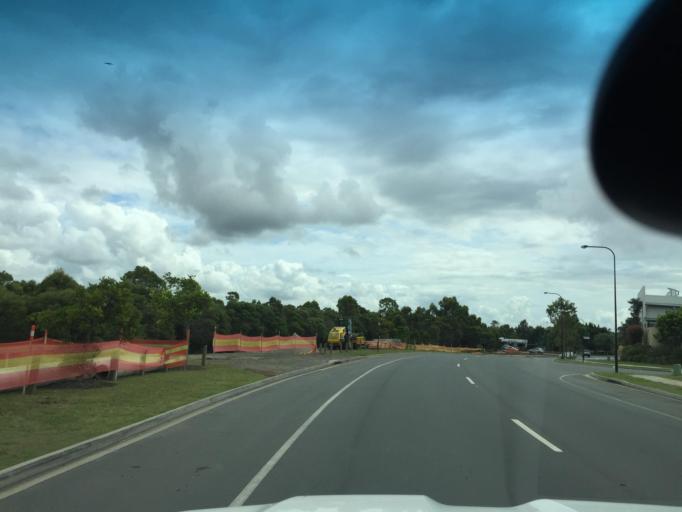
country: AU
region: Queensland
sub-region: Moreton Bay
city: Deception Bay
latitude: -27.2163
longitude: 152.9971
